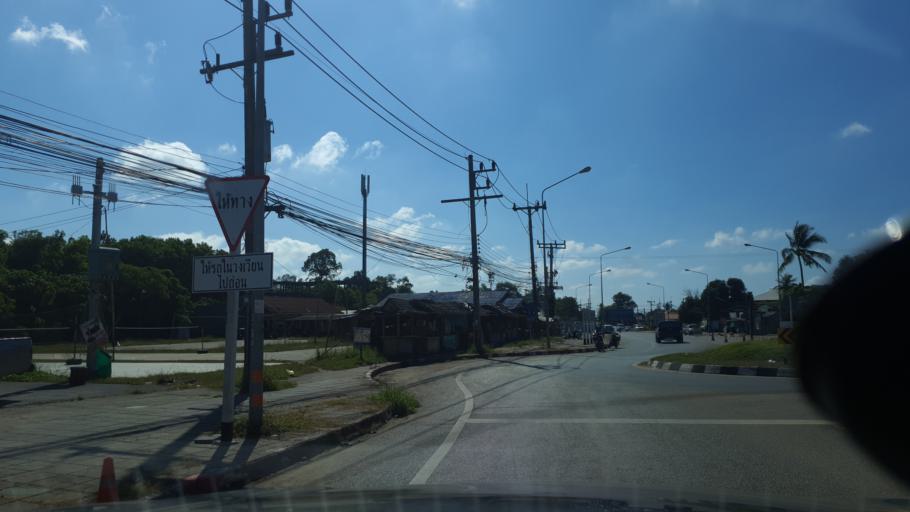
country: TH
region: Phangnga
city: Ban Ao Nang
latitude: 8.0331
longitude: 98.8617
